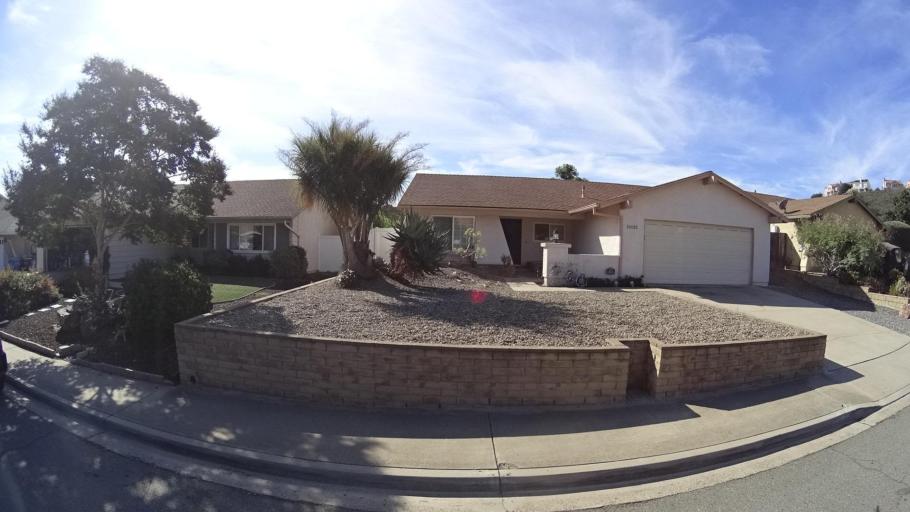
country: US
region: California
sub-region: San Diego County
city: La Presa
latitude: 32.7272
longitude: -116.9725
